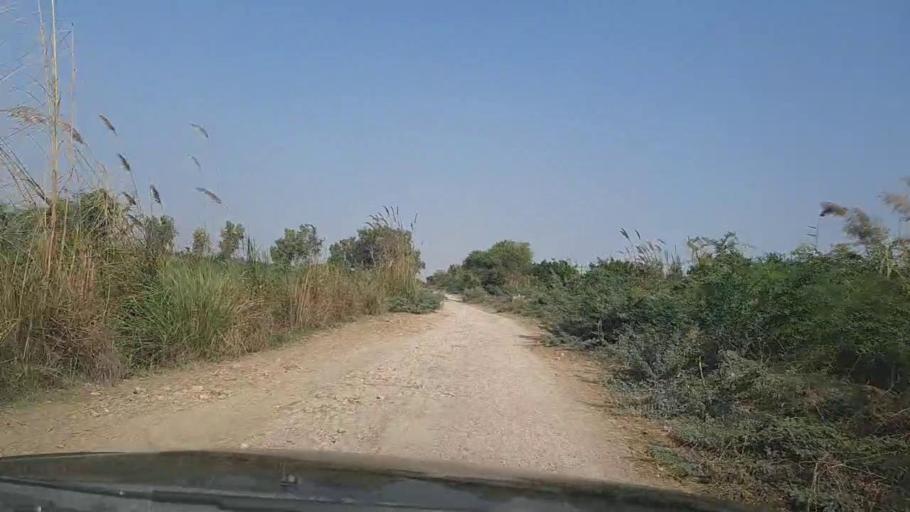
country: PK
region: Sindh
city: Thatta
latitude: 24.6325
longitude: 67.8134
